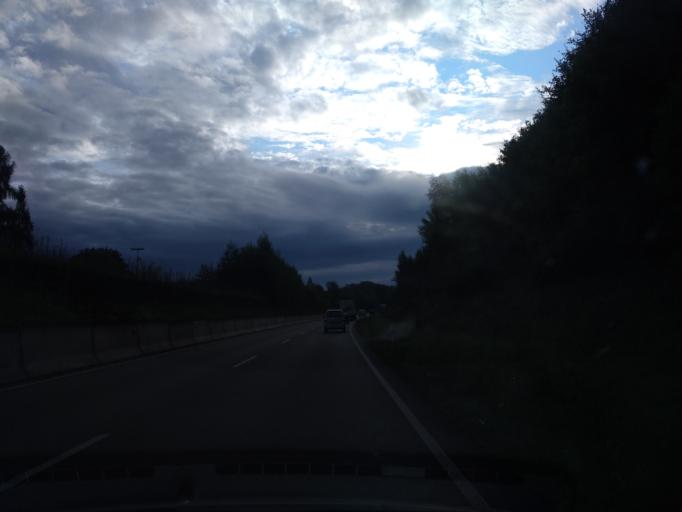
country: DE
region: Bavaria
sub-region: Upper Bavaria
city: Oberhausen
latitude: 48.7171
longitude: 11.0914
